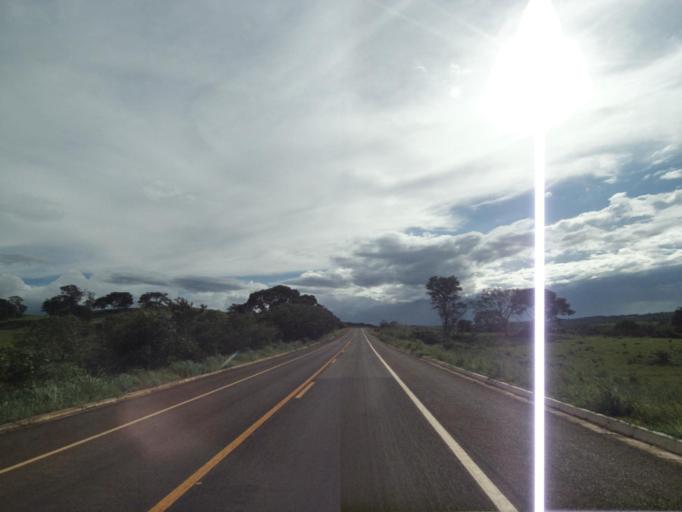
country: BR
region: Goias
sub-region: Jaragua
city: Jaragua
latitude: -15.8936
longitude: -49.5183
